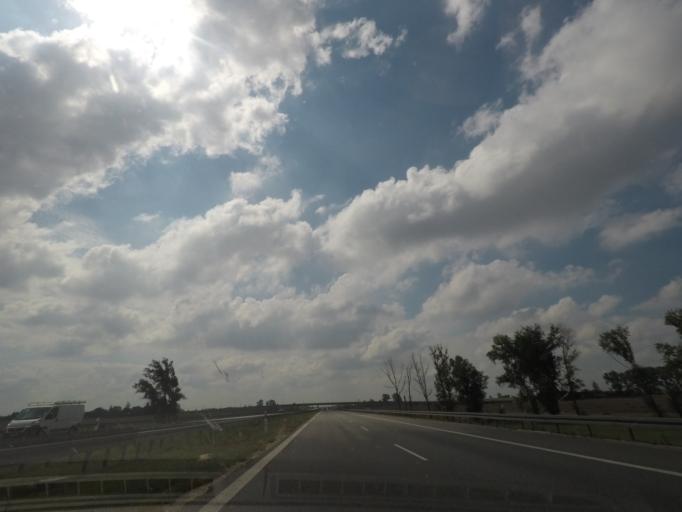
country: PL
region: Lodz Voivodeship
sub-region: Powiat kutnowski
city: Krzyzanow
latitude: 52.1733
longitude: 19.4854
